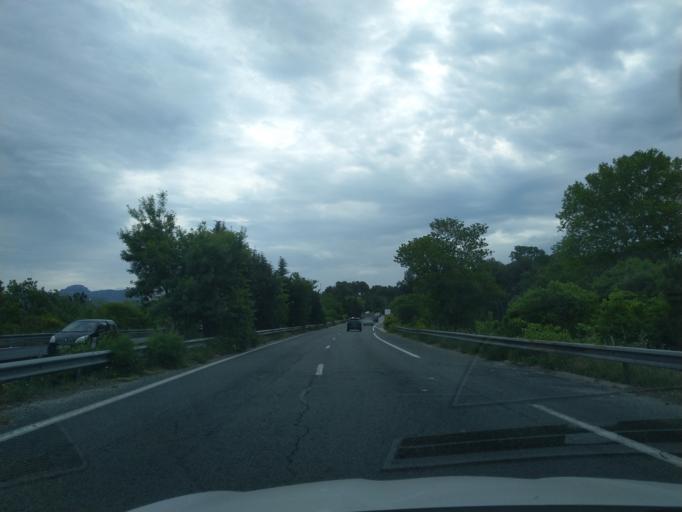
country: FR
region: Provence-Alpes-Cote d'Azur
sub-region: Departement des Bouches-du-Rhone
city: Aubagne
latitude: 43.2899
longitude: 5.5557
